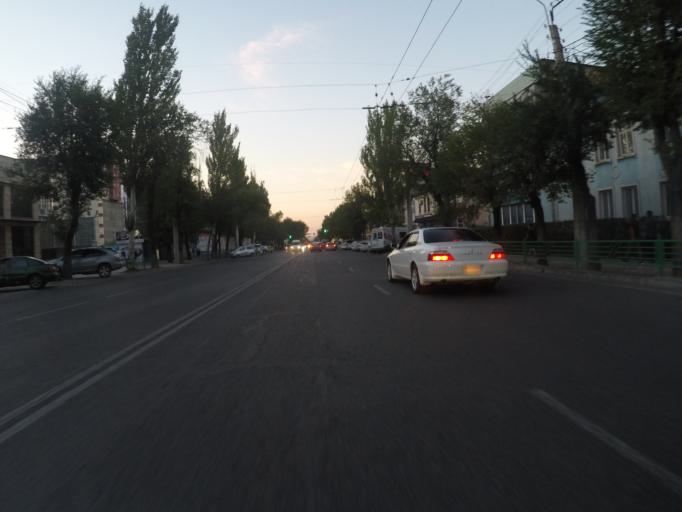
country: KG
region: Chuy
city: Bishkek
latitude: 42.8554
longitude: 74.6101
